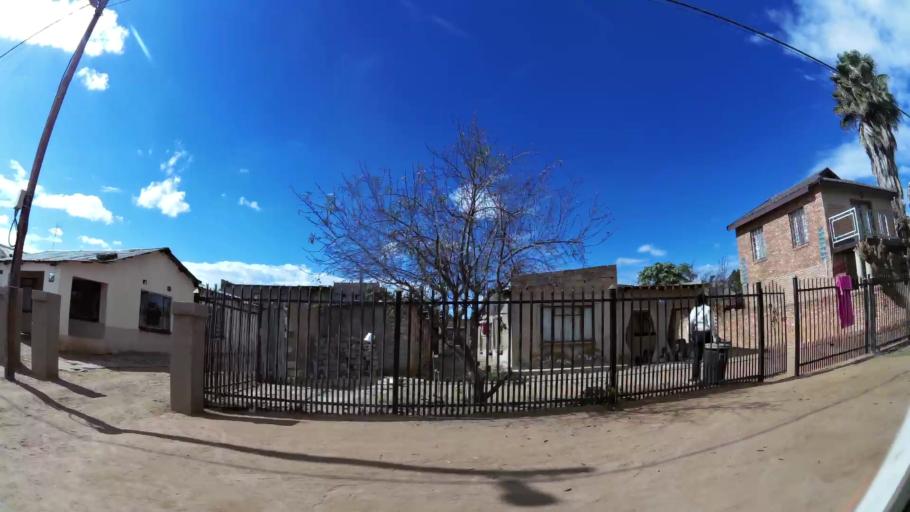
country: ZA
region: Limpopo
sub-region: Waterberg District Municipality
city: Bela-Bela
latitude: -24.8866
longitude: 28.3147
